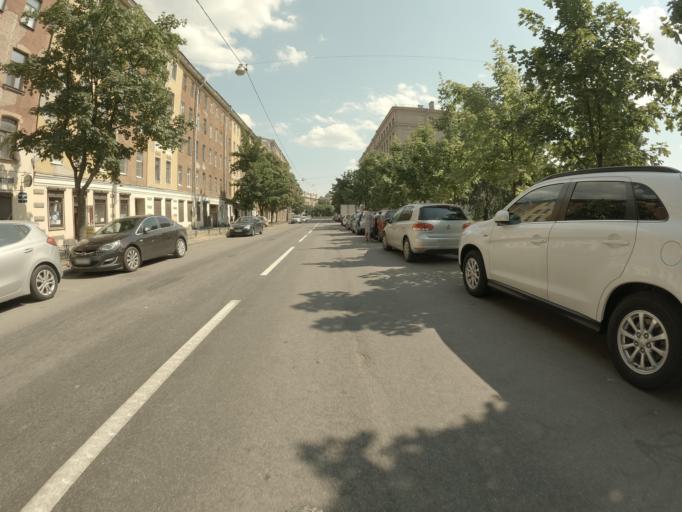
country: RU
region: St.-Petersburg
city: Admiralteisky
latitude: 59.9022
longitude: 30.2707
